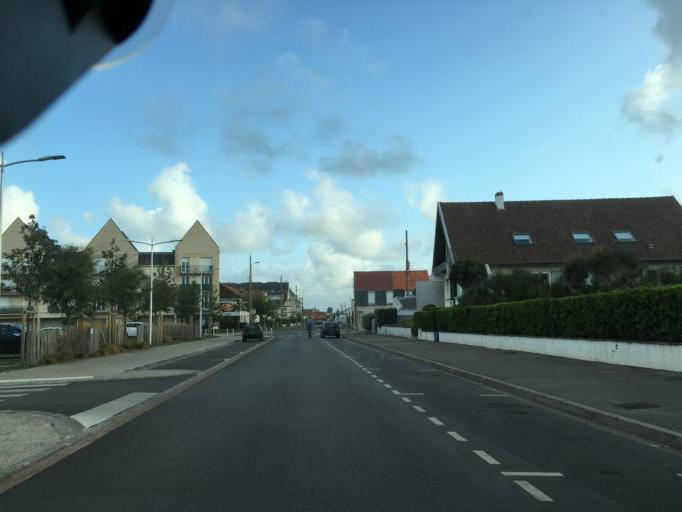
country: FR
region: Nord-Pas-de-Calais
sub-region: Departement du Pas-de-Calais
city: Berck-Plage
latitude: 50.4087
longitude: 1.5685
